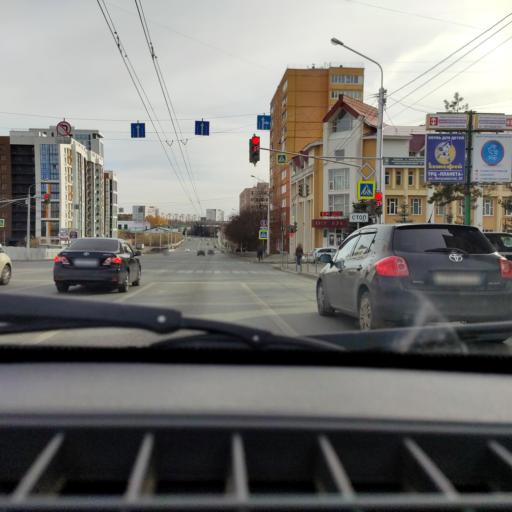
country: RU
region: Bashkortostan
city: Ufa
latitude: 54.7573
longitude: 56.0246
